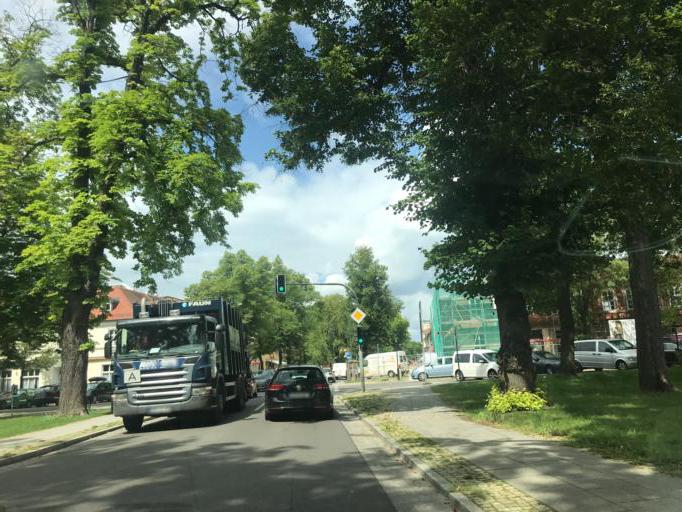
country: DE
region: Brandenburg
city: Rheinsberg
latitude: 53.0999
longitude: 12.8913
